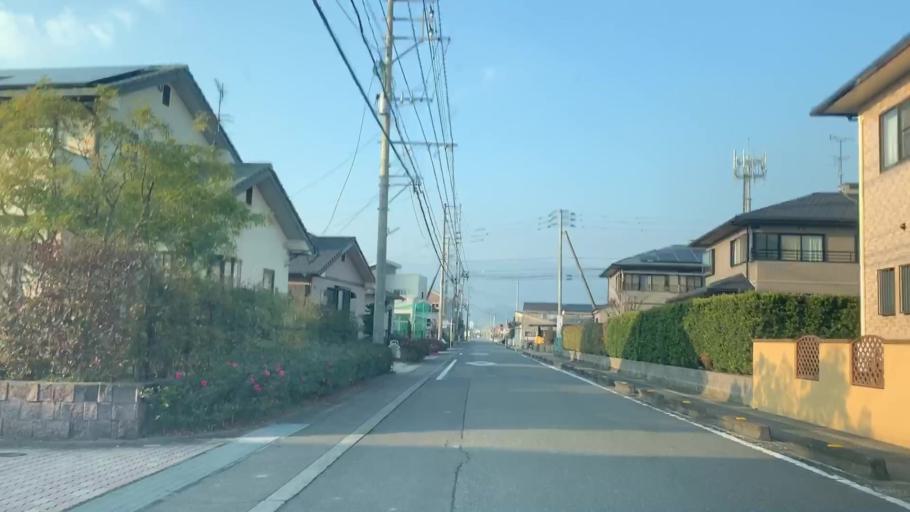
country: JP
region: Saga Prefecture
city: Saga-shi
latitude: 33.2716
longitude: 130.2290
